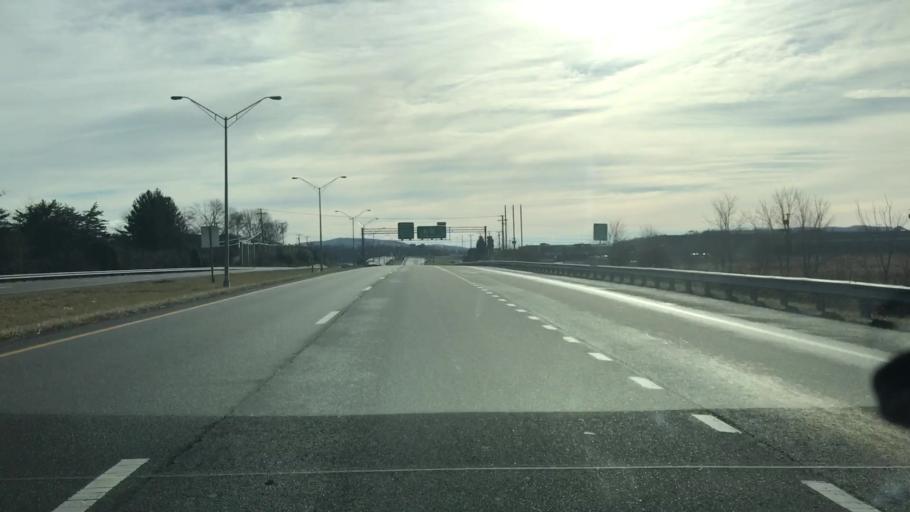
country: US
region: Virginia
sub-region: Montgomery County
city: Christiansburg
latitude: 37.1374
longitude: -80.3794
